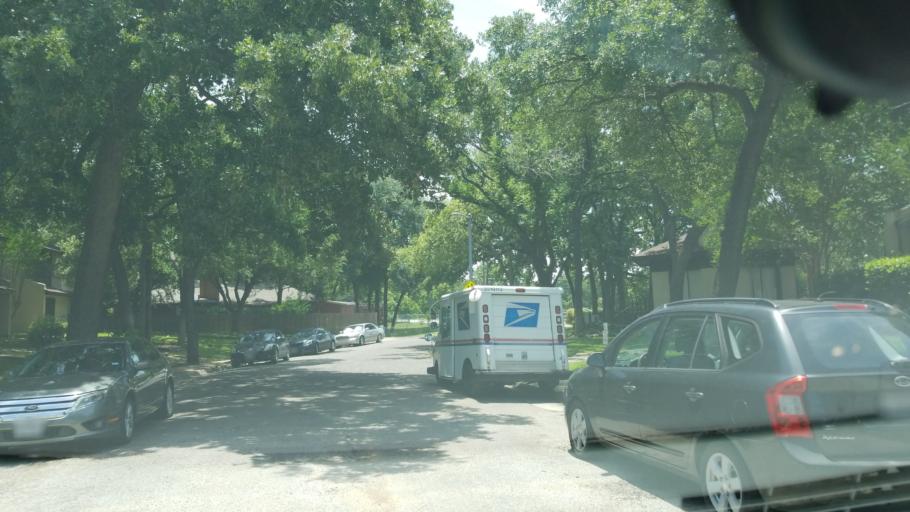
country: US
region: Texas
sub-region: Dallas County
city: Irving
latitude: 32.8192
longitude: -96.9520
